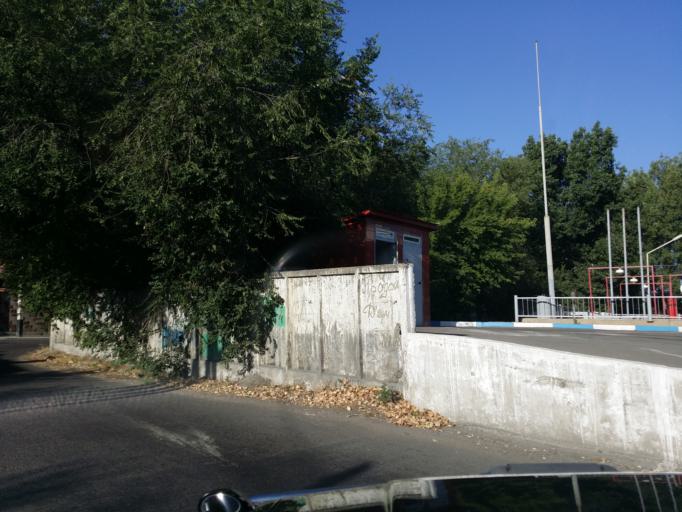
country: KZ
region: Almaty Oblysy
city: Pervomayskiy
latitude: 43.3386
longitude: 76.9339
